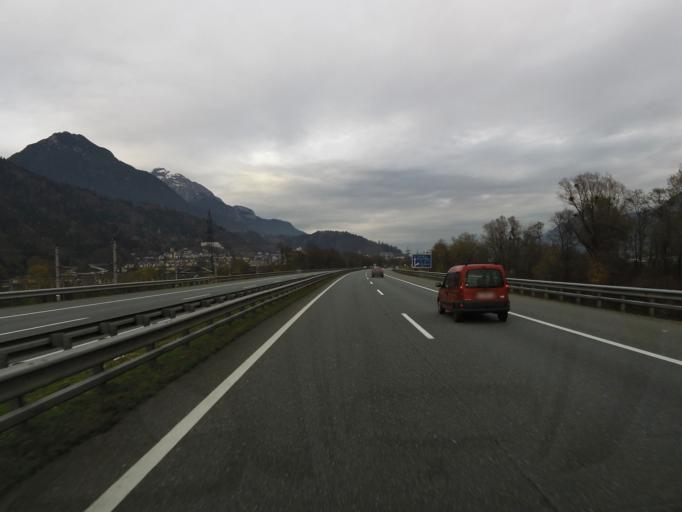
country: AT
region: Tyrol
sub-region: Politischer Bezirk Schwaz
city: Buch bei Jenbach
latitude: 47.3815
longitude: 11.7545
